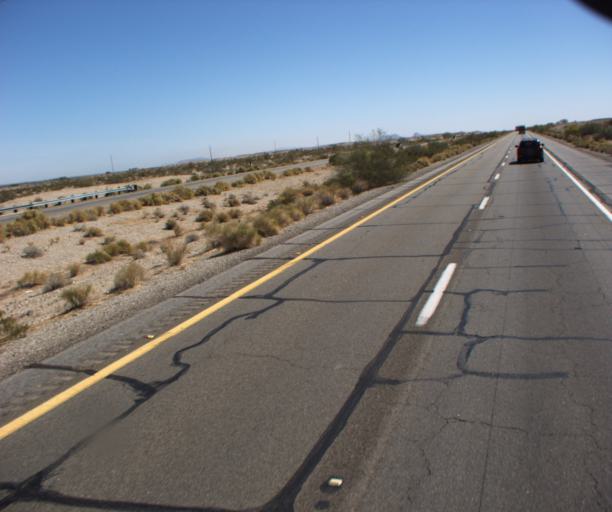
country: US
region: Arizona
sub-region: Yuma County
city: Wellton
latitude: 32.6581
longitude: -114.2478
